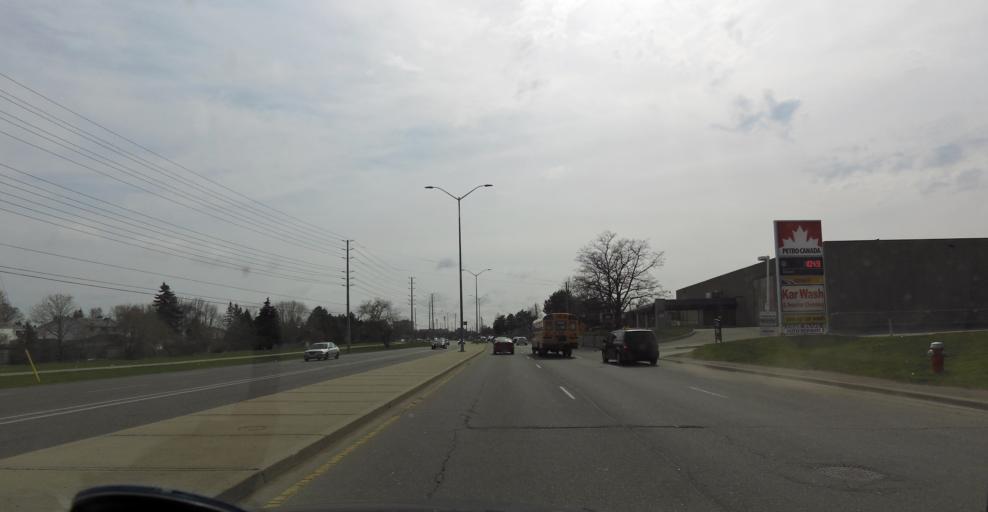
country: CA
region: Ontario
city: Mississauga
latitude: 43.5884
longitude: -79.5926
